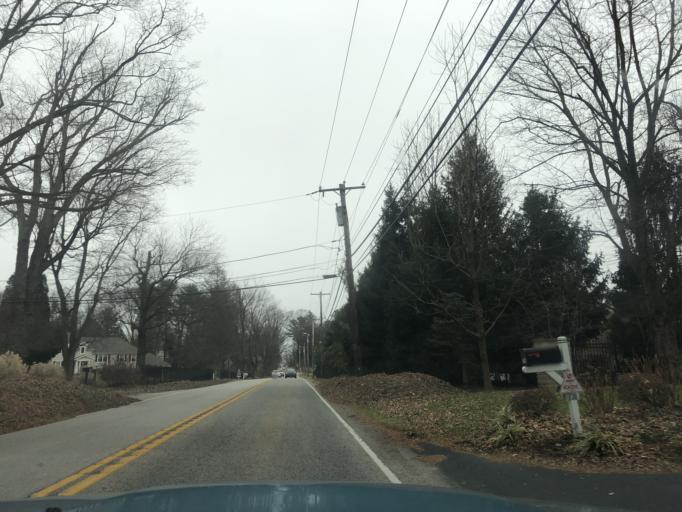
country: US
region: Pennsylvania
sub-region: Delaware County
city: Radnor
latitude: 40.0265
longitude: -75.3494
